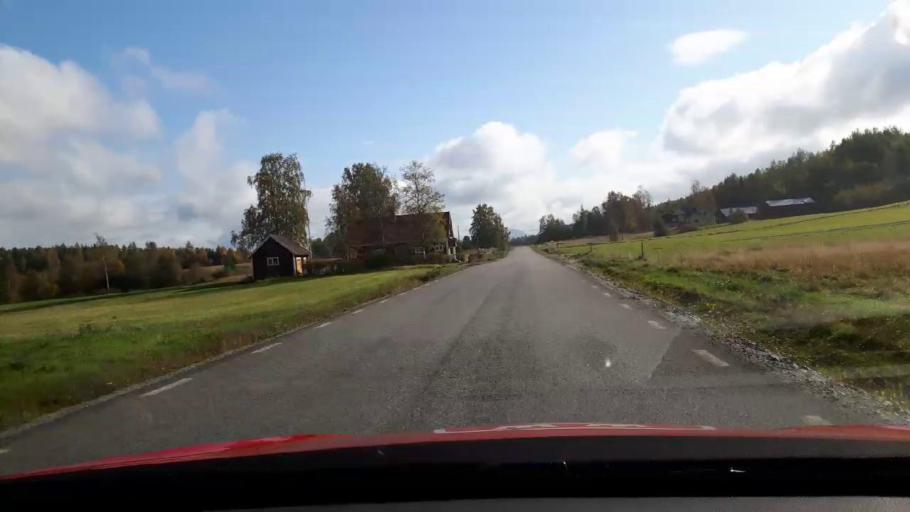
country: SE
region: Gaevleborg
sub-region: Ljusdals Kommun
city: Ljusdal
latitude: 61.7660
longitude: 16.0446
